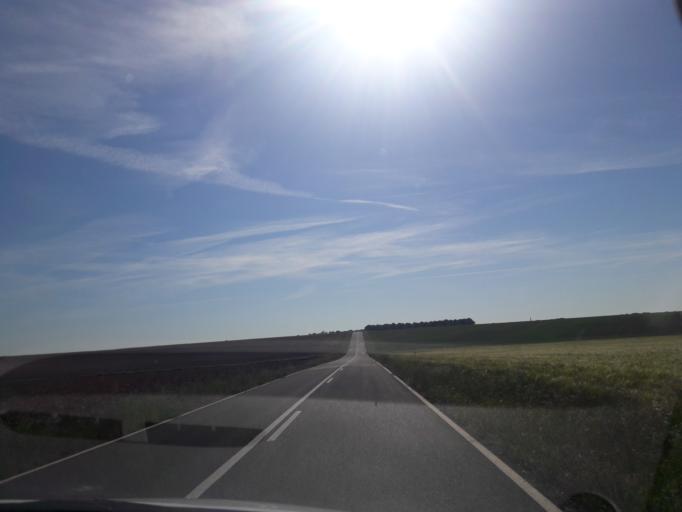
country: ES
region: Castille and Leon
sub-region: Provincia de Salamanca
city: Aldeanueva de Figueroa
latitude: 41.1371
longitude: -5.4992
